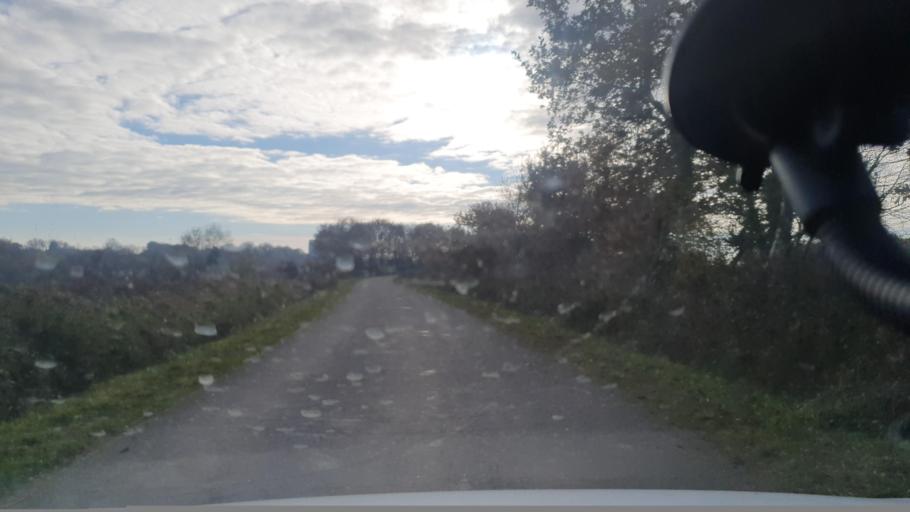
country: FR
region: Brittany
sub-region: Departement du Finistere
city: Briec
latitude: 48.1134
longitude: -4.0244
